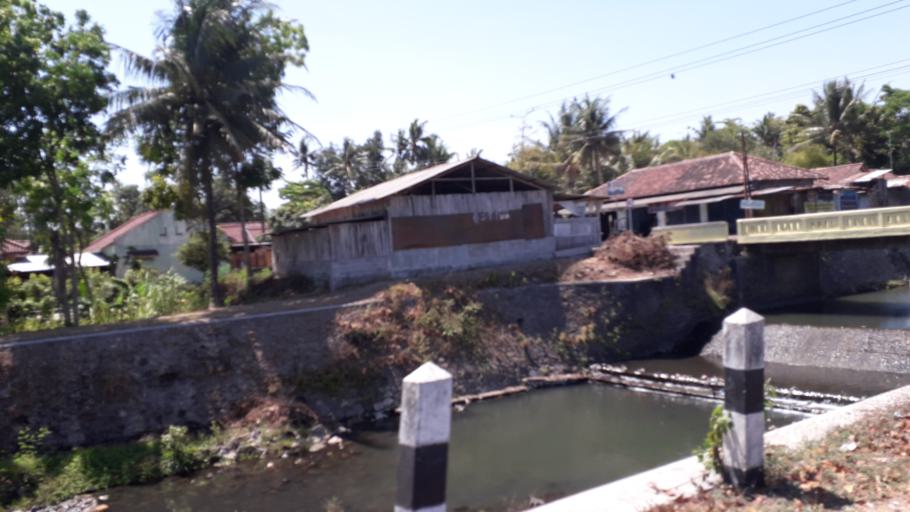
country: ID
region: Daerah Istimewa Yogyakarta
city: Pundong
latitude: -7.9573
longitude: 110.3242
